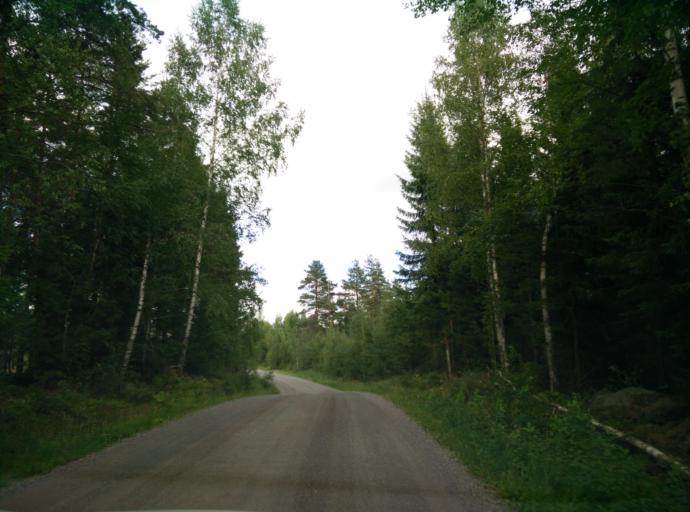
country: FI
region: Haeme
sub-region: Haemeenlinna
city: Kalvola
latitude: 61.1113
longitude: 24.1328
